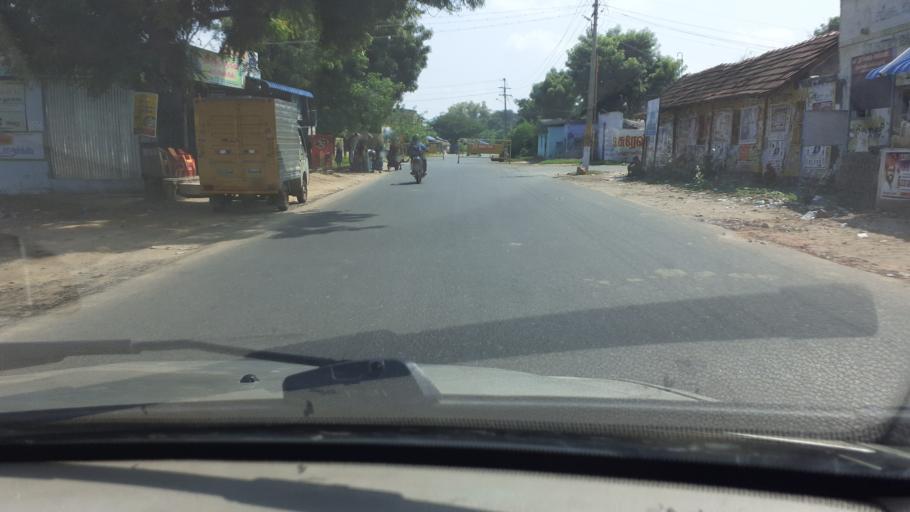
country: IN
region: Tamil Nadu
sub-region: Thoothukkudi
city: Srivaikuntam
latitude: 8.6327
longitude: 77.8990
